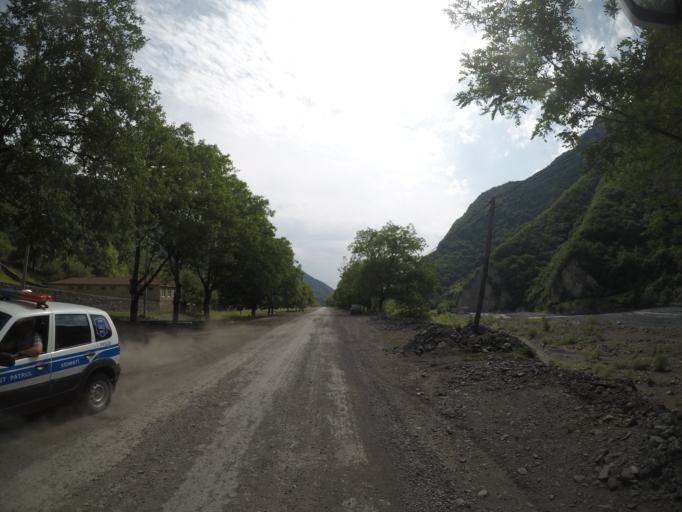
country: AZ
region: Qakh Rayon
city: Qaxbas
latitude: 41.4616
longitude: 47.0305
